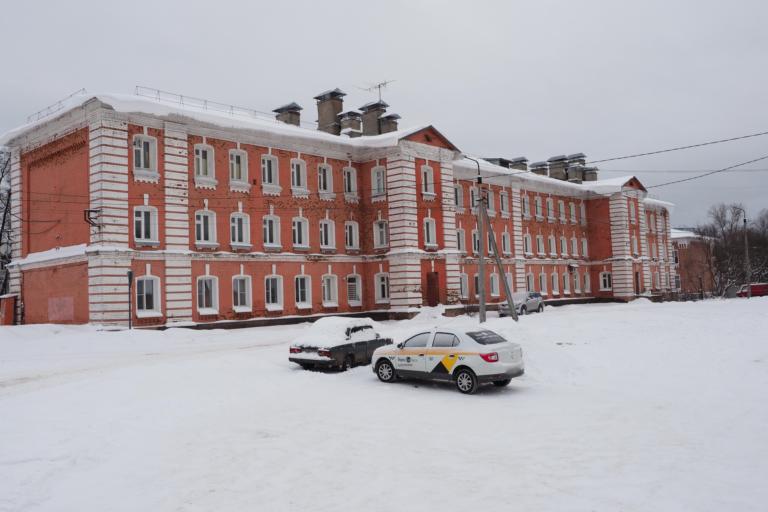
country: RU
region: Moskovskaya
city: Yegor'yevsk
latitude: 55.3812
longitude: 39.0274
